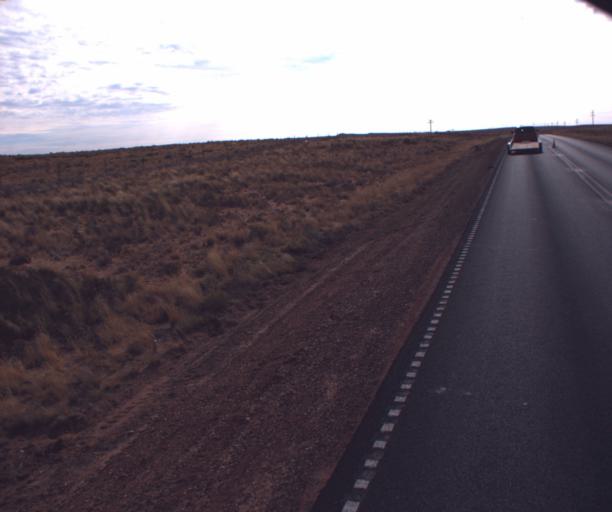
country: US
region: Arizona
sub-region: Apache County
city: Chinle
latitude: 36.0910
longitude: -109.6231
